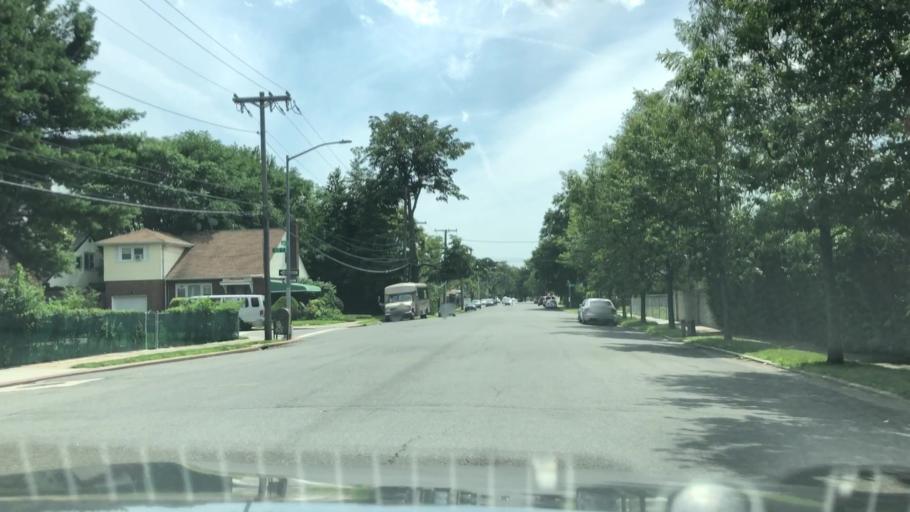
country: US
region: New York
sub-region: Queens County
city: Jamaica
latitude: 40.6988
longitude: -73.7747
